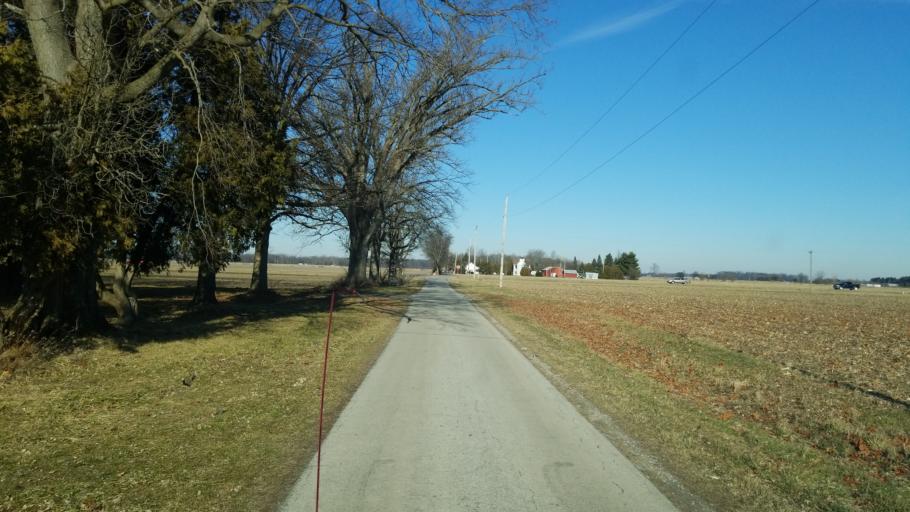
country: US
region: Ohio
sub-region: Henry County
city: Liberty Center
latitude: 41.3697
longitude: -83.9802
